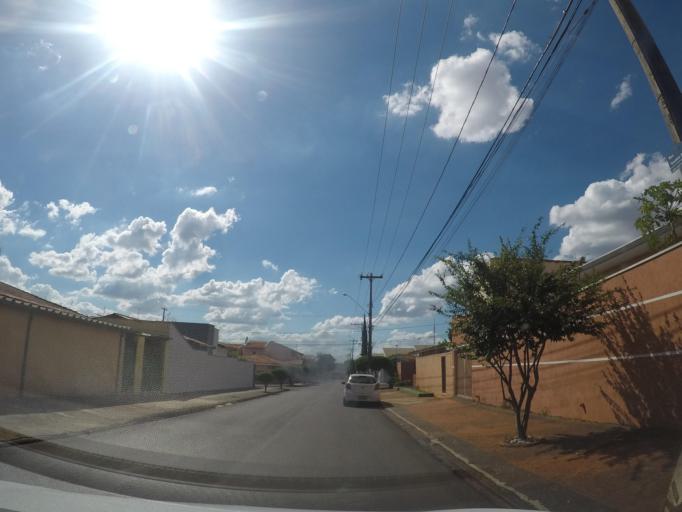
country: BR
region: Sao Paulo
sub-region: Sumare
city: Sumare
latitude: -22.8337
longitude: -47.2744
